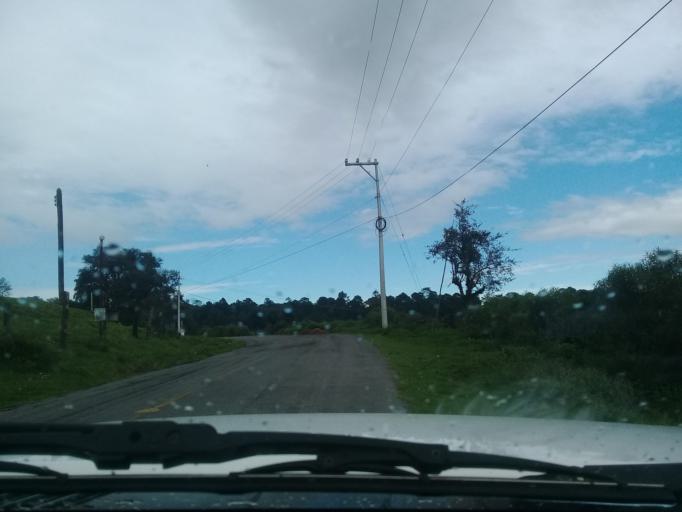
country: MX
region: Veracruz
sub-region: Acajete
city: La Joya
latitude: 19.6137
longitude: -97.0063
